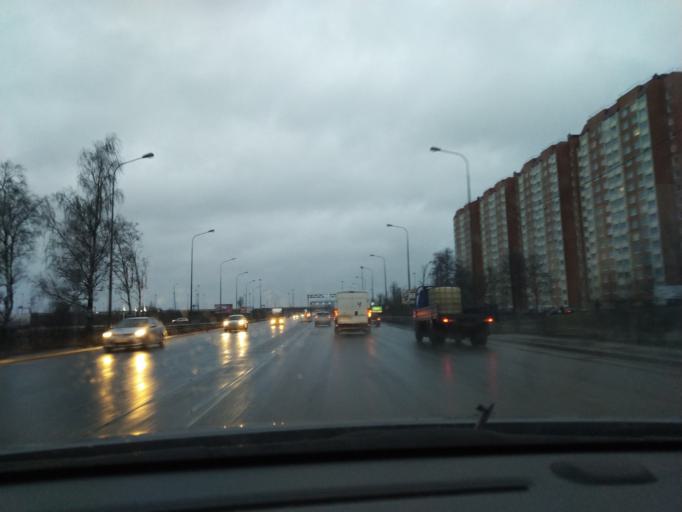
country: RU
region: St.-Petersburg
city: Gorelovo
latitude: 59.7942
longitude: 30.1499
